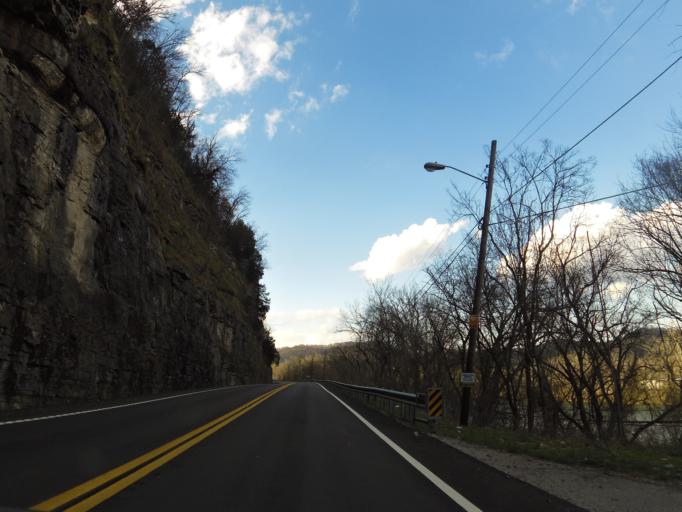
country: US
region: Tennessee
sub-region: Smith County
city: Carthage
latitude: 36.2503
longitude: -85.9578
